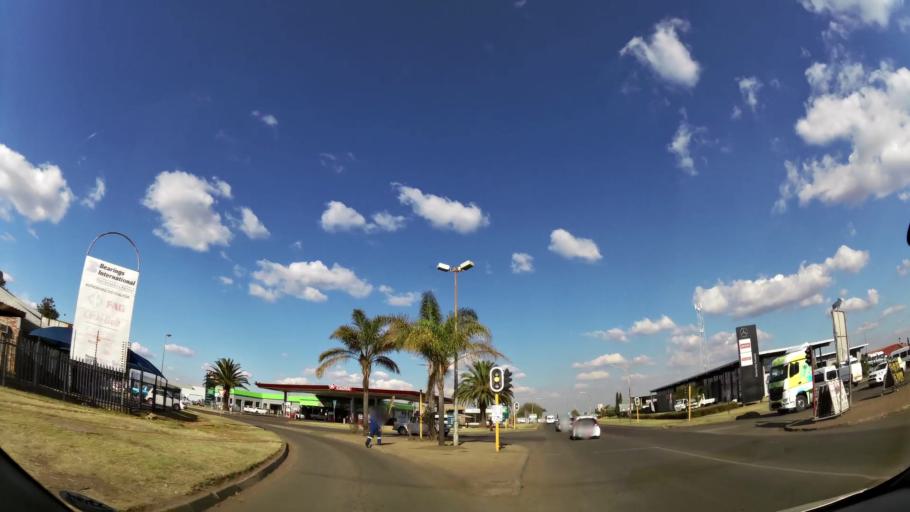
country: ZA
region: Mpumalanga
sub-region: Nkangala District Municipality
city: Witbank
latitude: -25.8935
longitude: 29.2278
